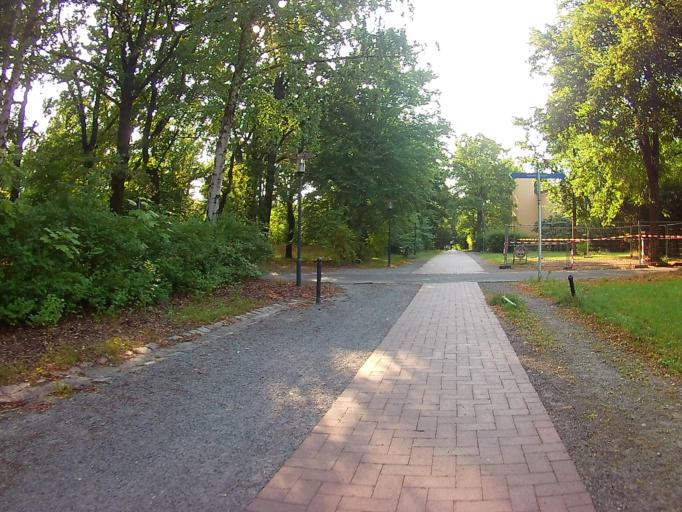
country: DE
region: Berlin
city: Biesdorf
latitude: 52.5151
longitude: 13.5679
